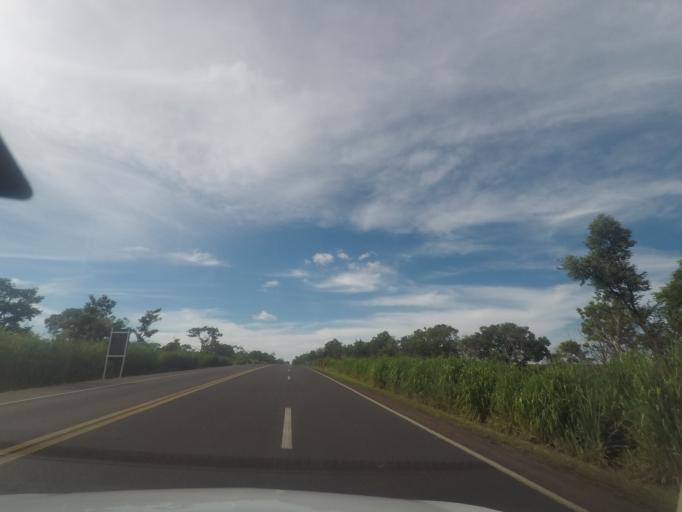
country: BR
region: Minas Gerais
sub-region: Monte Alegre De Minas
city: Monte Alegre de Minas
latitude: -18.9903
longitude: -49.0214
